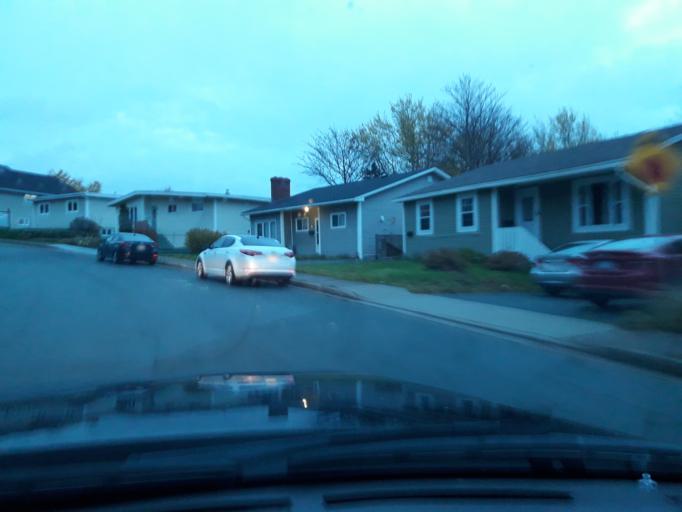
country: CA
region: Newfoundland and Labrador
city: St. John's
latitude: 47.5687
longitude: -52.7481
